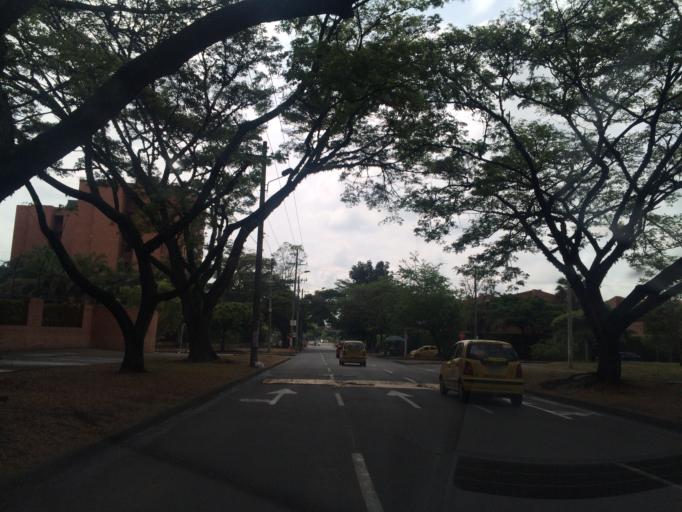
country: CO
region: Valle del Cauca
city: Cali
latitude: 3.3795
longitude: -76.5274
